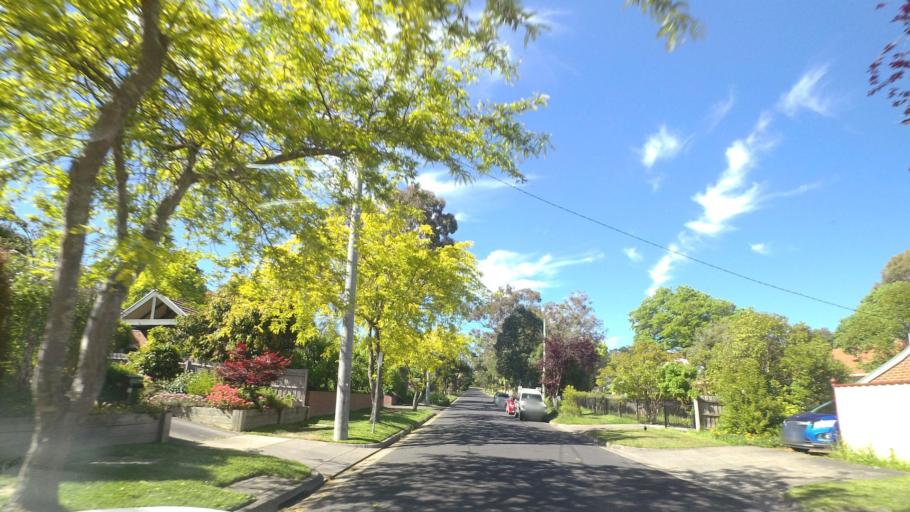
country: AU
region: Victoria
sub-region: Maroondah
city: Ringwood East
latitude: -37.8176
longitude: 145.2524
